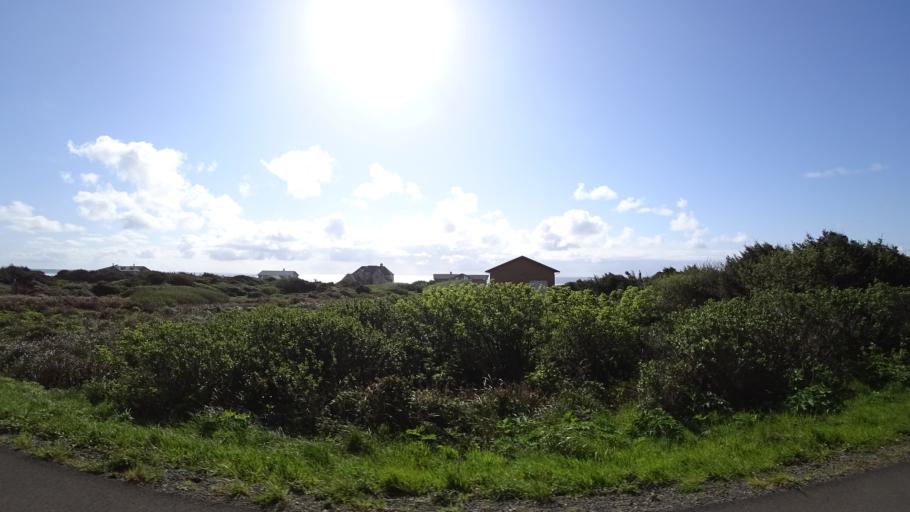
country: US
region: Oregon
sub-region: Lincoln County
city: Waldport
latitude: 44.2287
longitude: -124.1094
